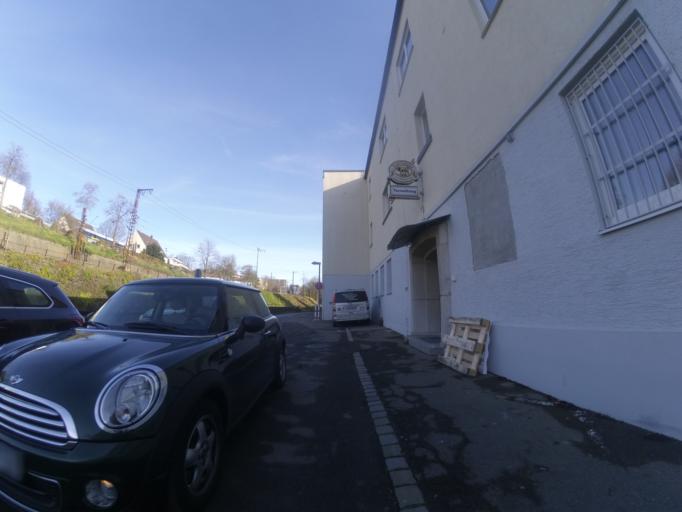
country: DE
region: Baden-Wuerttemberg
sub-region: Tuebingen Region
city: Ulm
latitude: 48.4071
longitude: 9.9894
